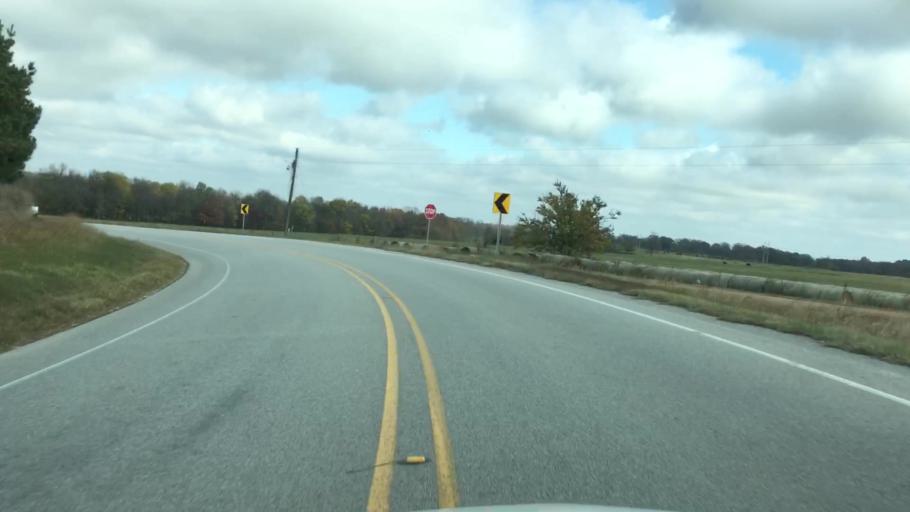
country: US
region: Arkansas
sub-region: Benton County
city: Centerton
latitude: 36.2873
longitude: -94.3459
